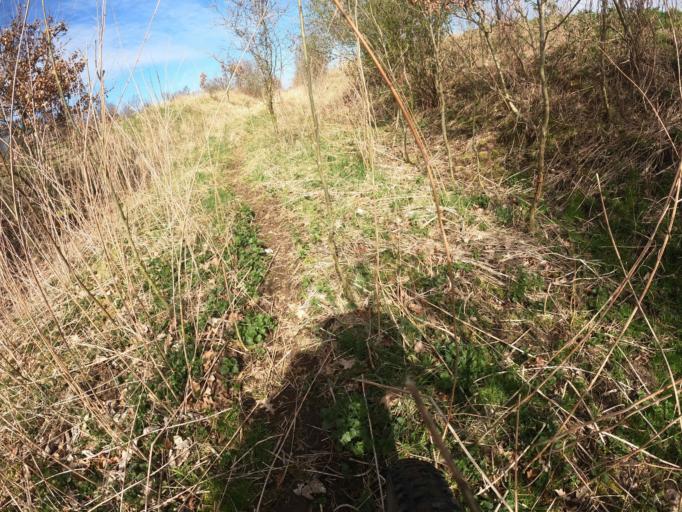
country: PL
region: West Pomeranian Voivodeship
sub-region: Powiat gryficki
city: Brojce
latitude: 53.9717
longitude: 15.3823
